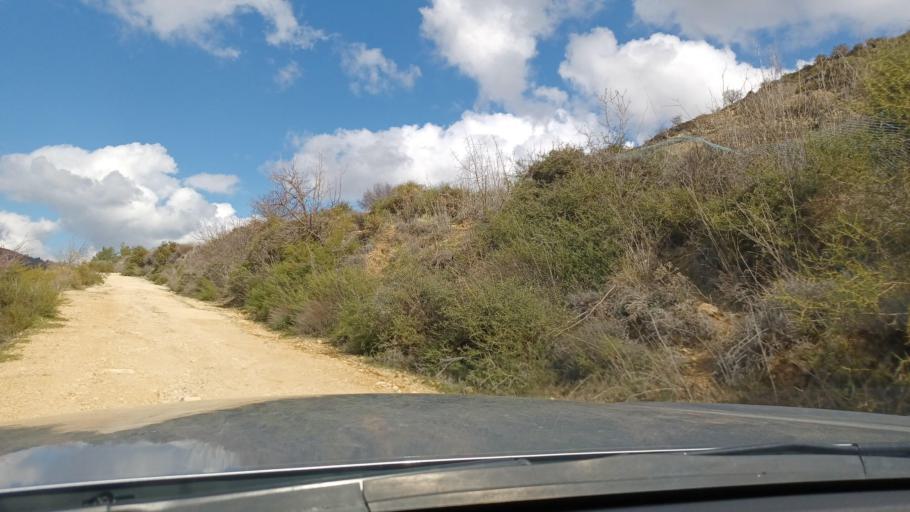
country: CY
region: Limassol
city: Pachna
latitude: 34.8301
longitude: 32.7618
